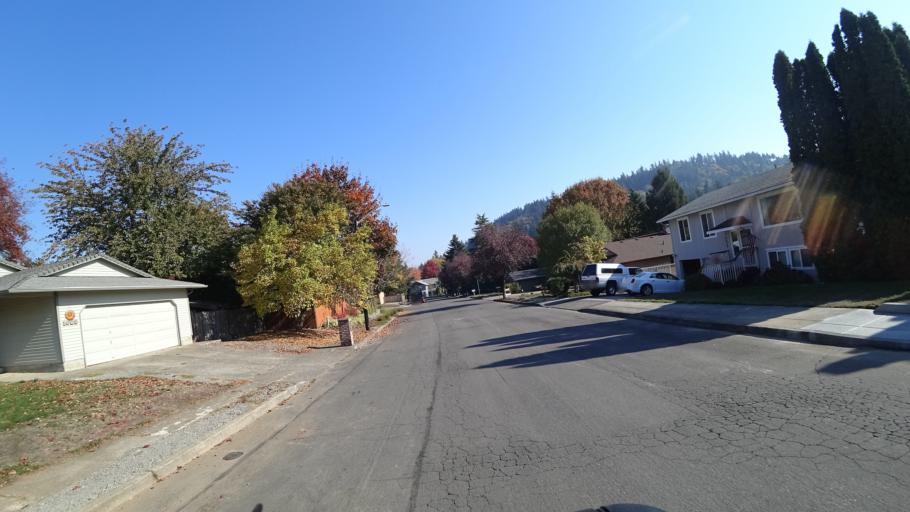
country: US
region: Oregon
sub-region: Multnomah County
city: Gresham
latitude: 45.4924
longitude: -122.4488
